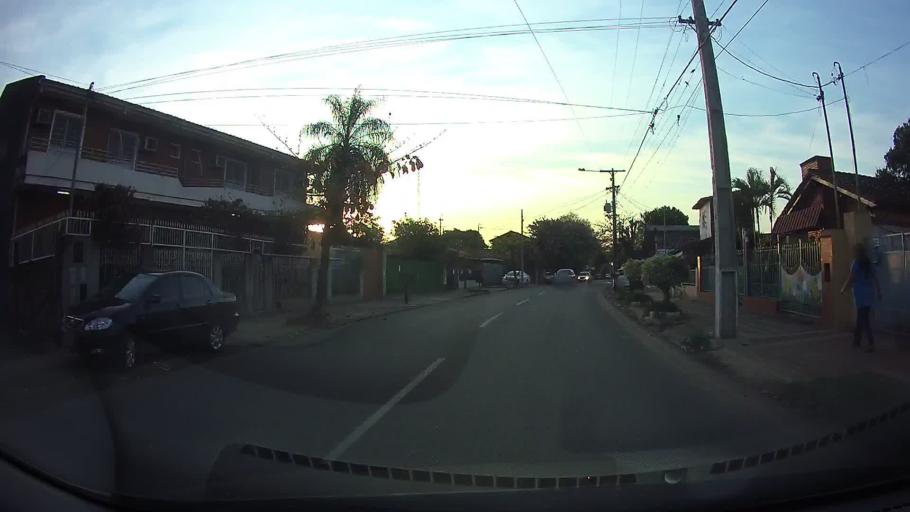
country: PY
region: Central
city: Lambare
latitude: -25.3212
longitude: -57.5756
